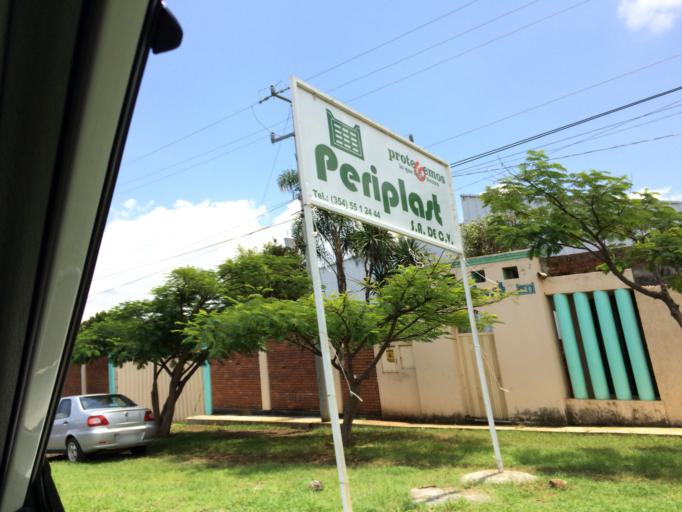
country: MX
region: Michoacan
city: Periban de Ramos
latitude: 19.5377
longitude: -102.4130
